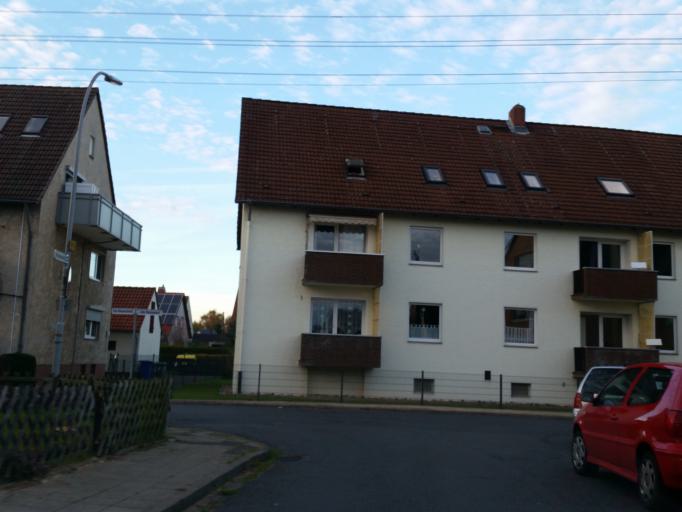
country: DE
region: Lower Saxony
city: Braunschweig
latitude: 52.2865
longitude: 10.5898
